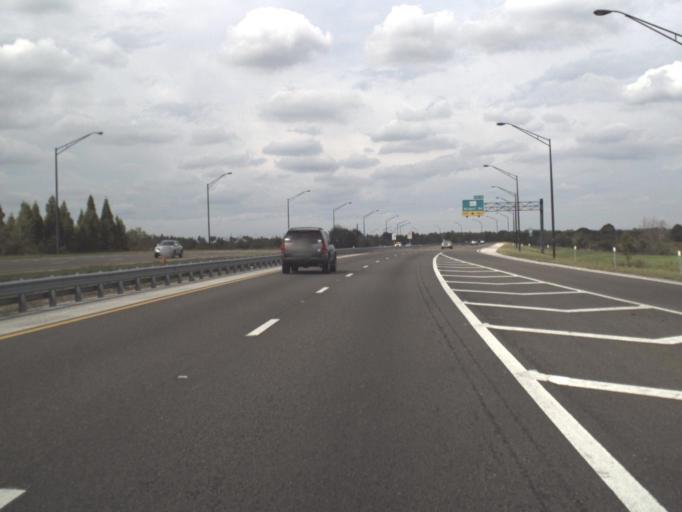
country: US
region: Florida
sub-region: Polk County
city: Winston
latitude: 28.0019
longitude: -82.0050
